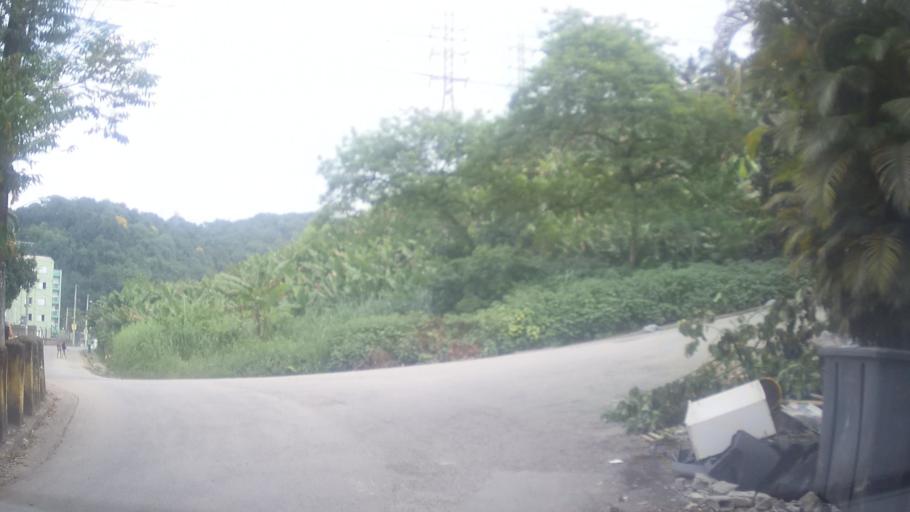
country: BR
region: Sao Paulo
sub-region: Santos
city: Santos
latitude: -23.9417
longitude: -46.3507
